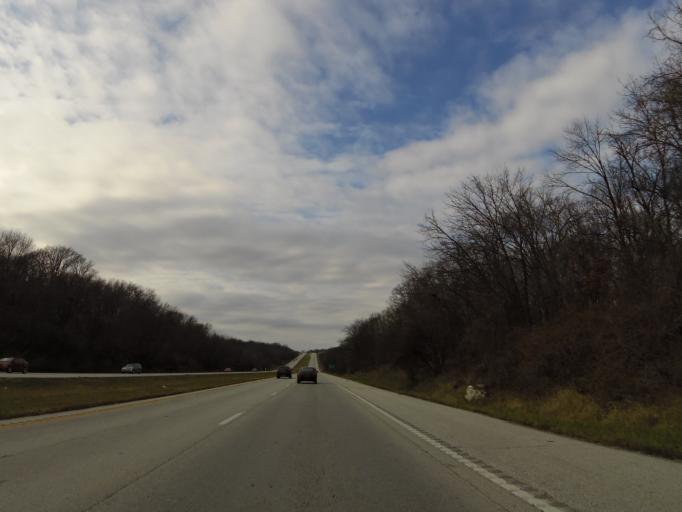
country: US
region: Missouri
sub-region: Marion County
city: Hannibal
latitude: 39.7346
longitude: -91.4061
